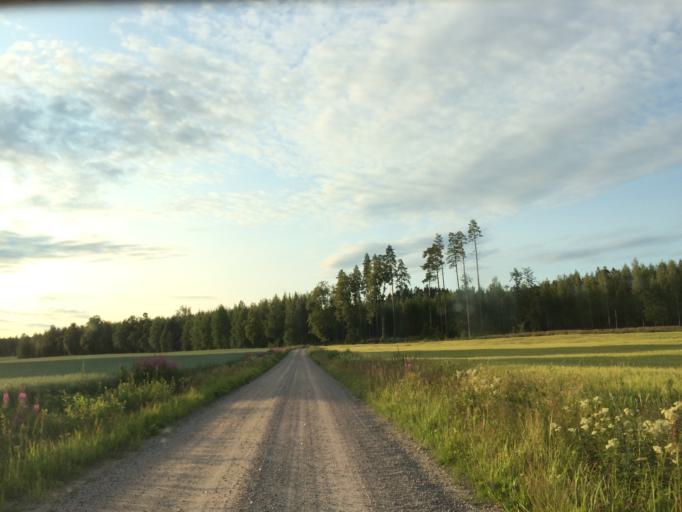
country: FI
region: Haeme
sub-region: Haemeenlinna
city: Janakkala
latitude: 60.8897
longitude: 24.6173
